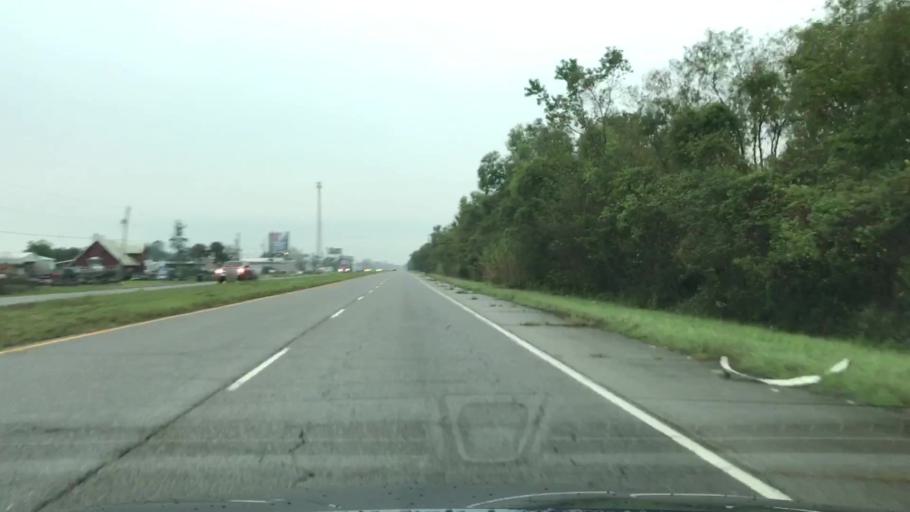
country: US
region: Louisiana
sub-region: Saint Charles Parish
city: Des Allemands
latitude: 29.8132
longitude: -90.4907
